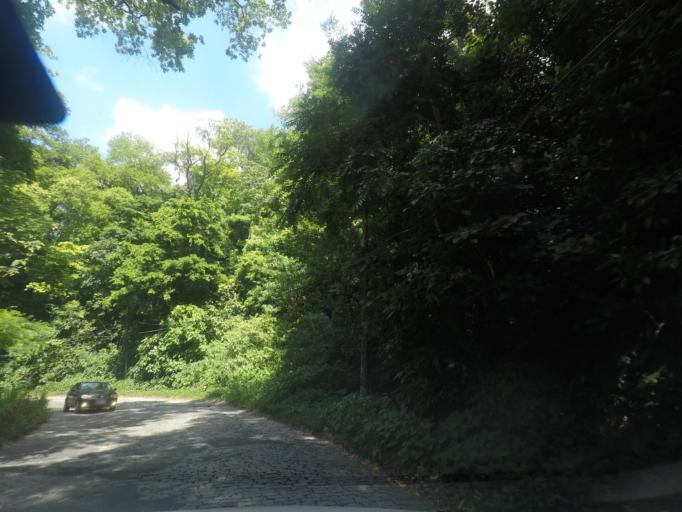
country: BR
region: Rio de Janeiro
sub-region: Petropolis
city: Petropolis
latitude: -22.5507
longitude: -43.1844
